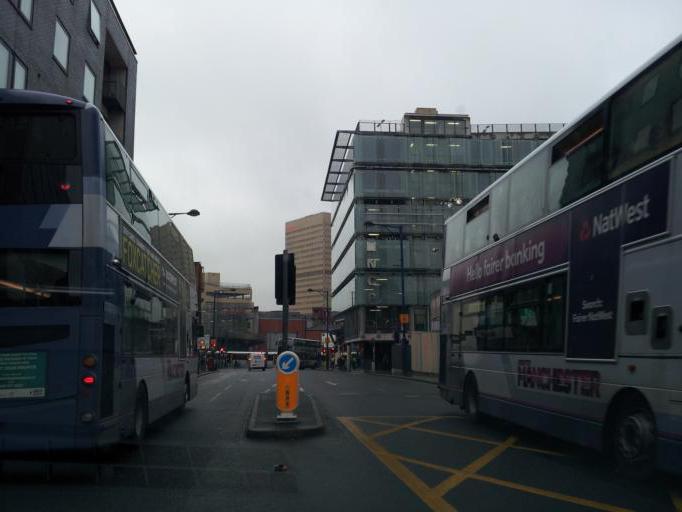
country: GB
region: England
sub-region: Manchester
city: Manchester
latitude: 53.4854
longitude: -2.2371
